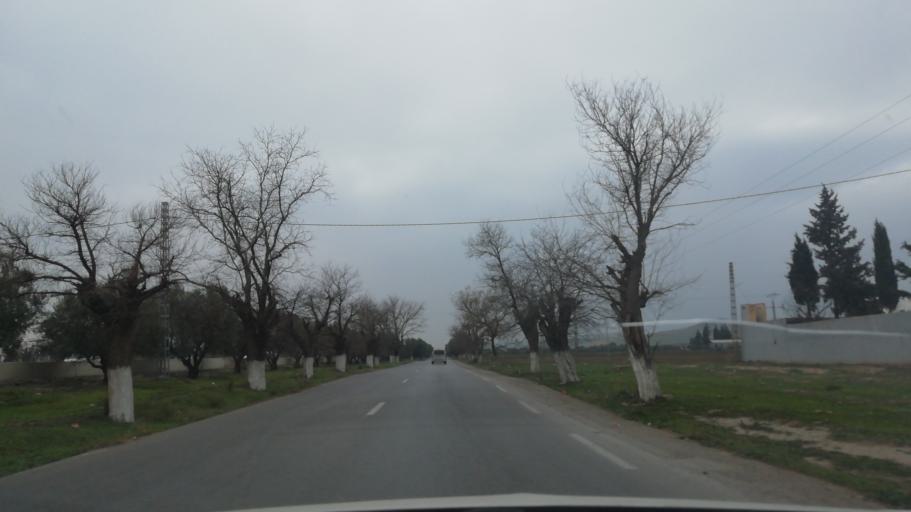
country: DZ
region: Sidi Bel Abbes
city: Sfizef
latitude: 35.2180
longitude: -0.3021
